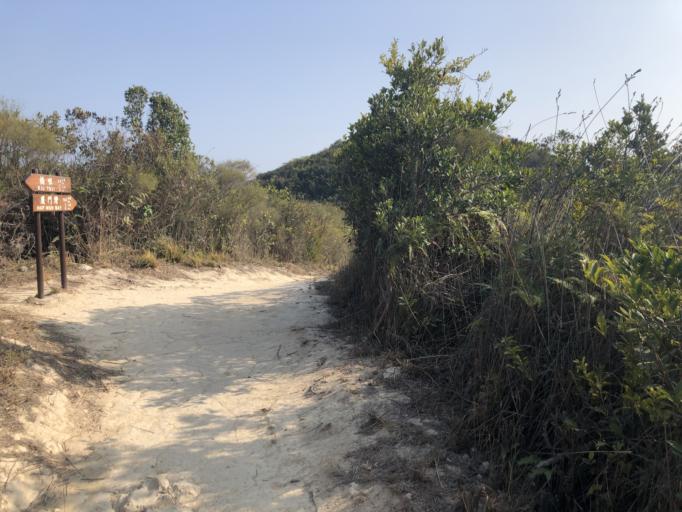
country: HK
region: Sai Kung
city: Sai Kung
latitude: 22.3632
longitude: 114.2933
